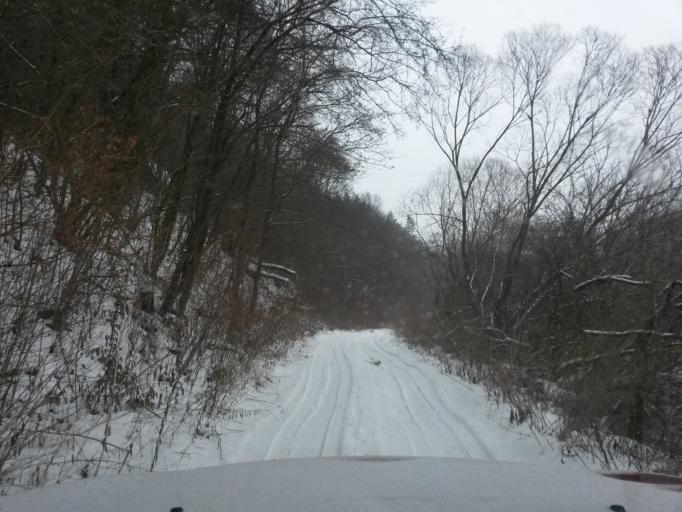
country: SK
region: Presovsky
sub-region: Okres Presov
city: Presov
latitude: 48.8981
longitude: 21.2030
